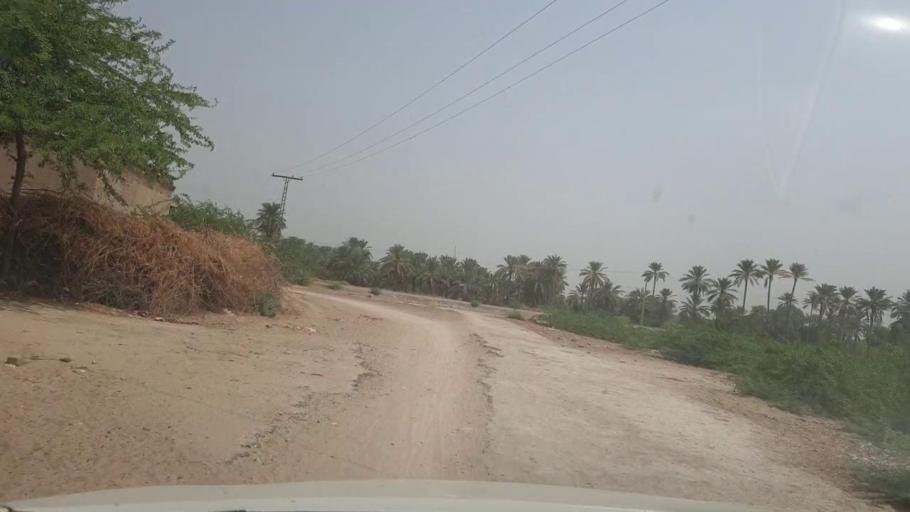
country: PK
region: Sindh
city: Kot Diji
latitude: 27.3481
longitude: 68.7178
